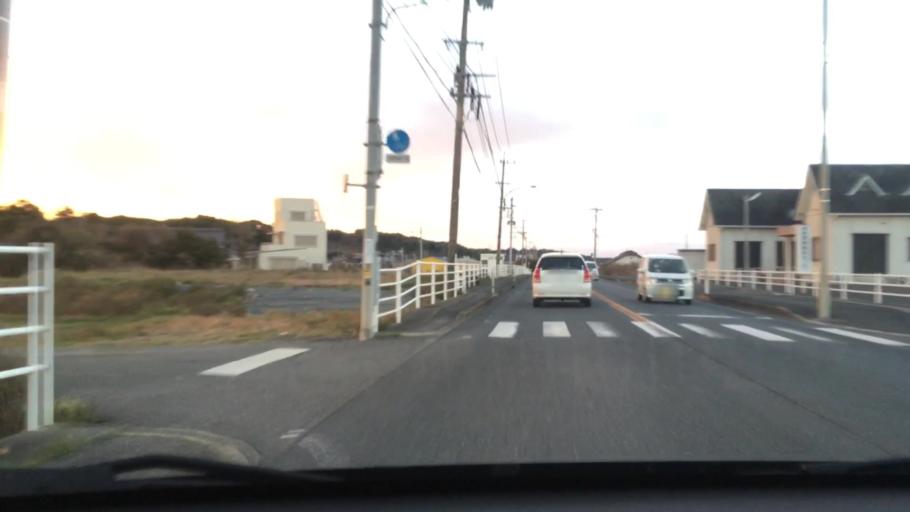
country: JP
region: Fukuoka
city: Shiida
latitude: 33.6303
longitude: 131.0841
